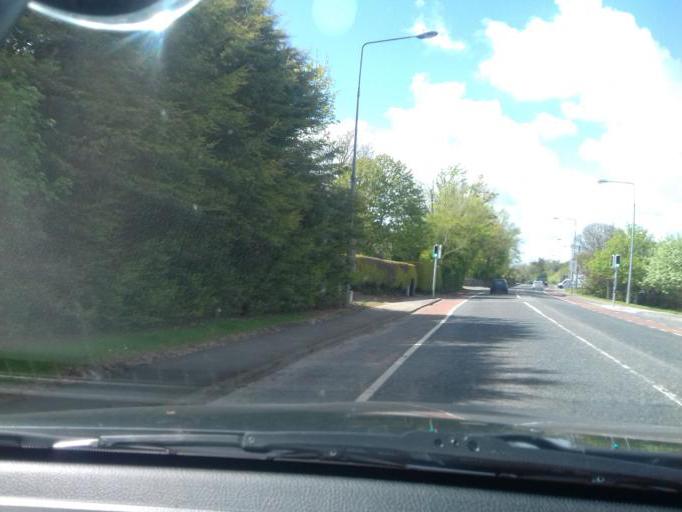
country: IE
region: Munster
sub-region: Waterford
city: Waterford
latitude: 52.2375
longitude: -7.0621
